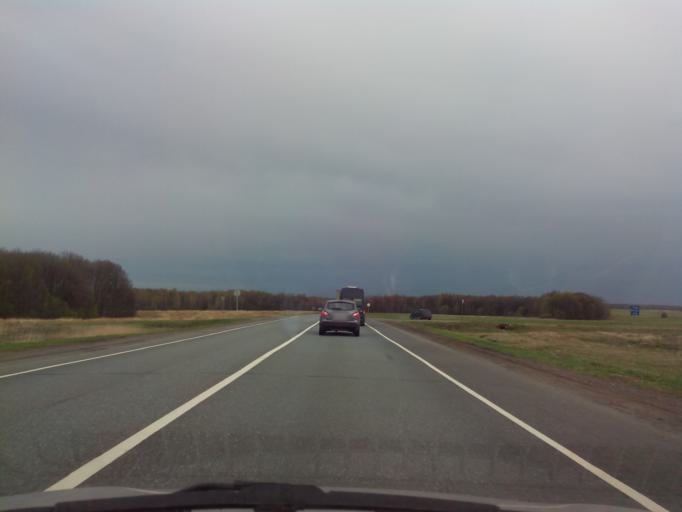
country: RU
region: Moskovskaya
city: Uzunovo
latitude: 54.5405
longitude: 38.4702
